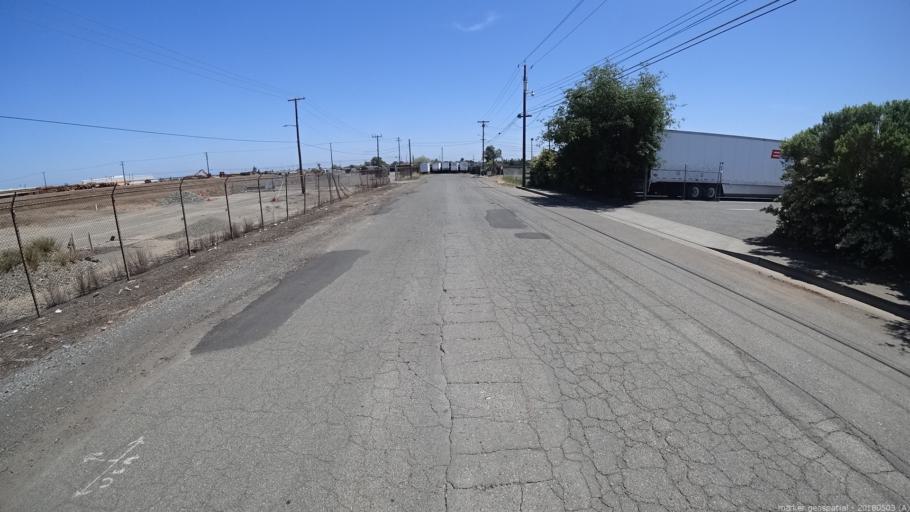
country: US
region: California
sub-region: Sacramento County
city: Arden-Arcade
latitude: 38.6398
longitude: -121.4076
